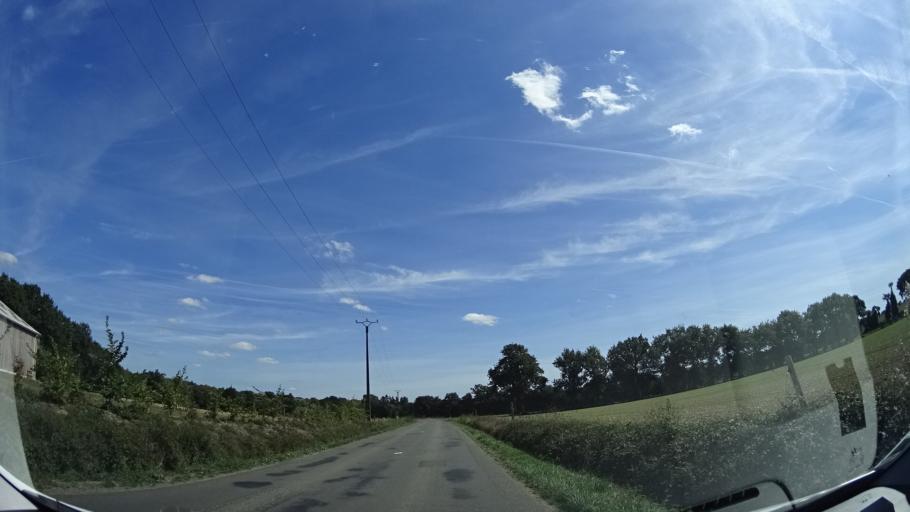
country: FR
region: Brittany
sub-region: Departement d'Ille-et-Vilaine
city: Chevaigne
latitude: 48.2099
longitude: -1.6424
